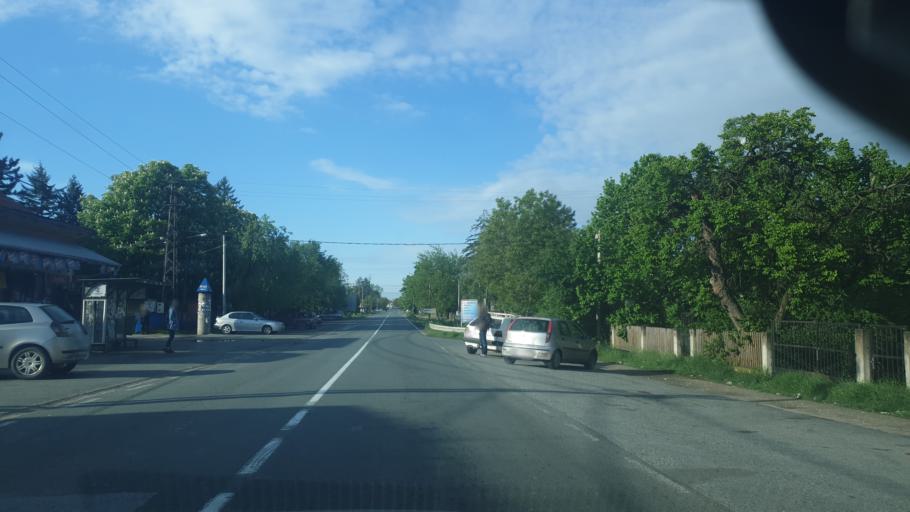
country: RS
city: Stubline
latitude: 44.5721
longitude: 20.1511
